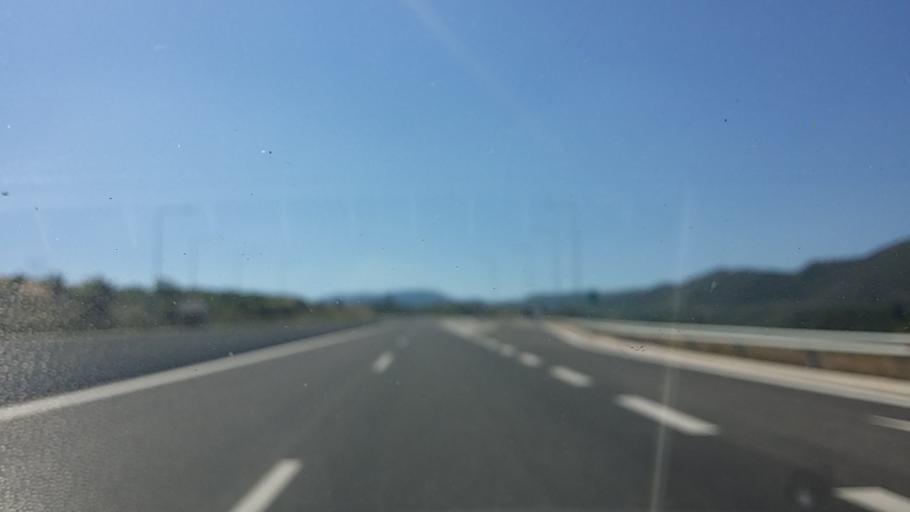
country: GR
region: Peloponnese
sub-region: Nomos Arkadias
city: Megalopoli
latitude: 37.3265
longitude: 22.1637
